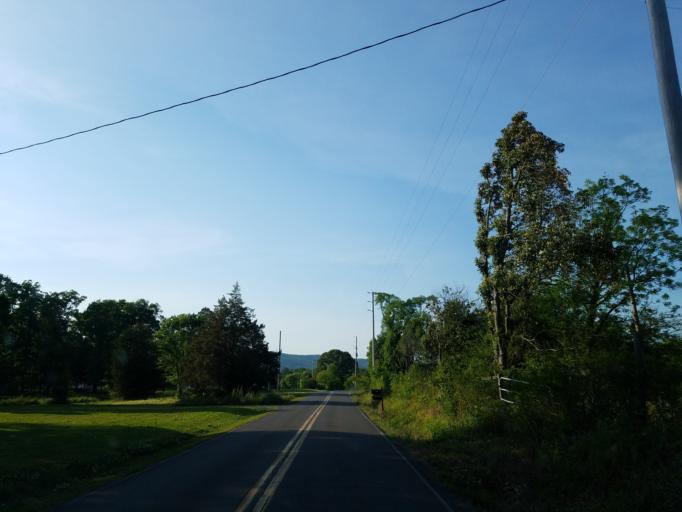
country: US
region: Georgia
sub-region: Gordon County
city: Calhoun
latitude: 34.5030
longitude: -85.1158
